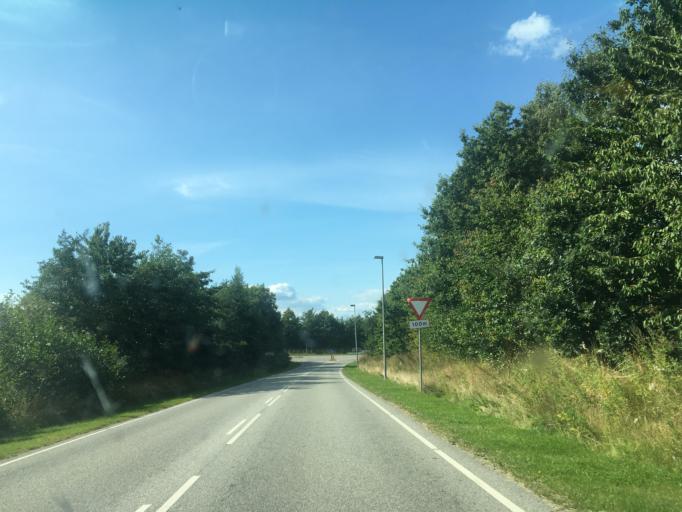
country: DK
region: South Denmark
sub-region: Middelfart Kommune
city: Ejby
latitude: 55.3973
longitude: 9.9669
